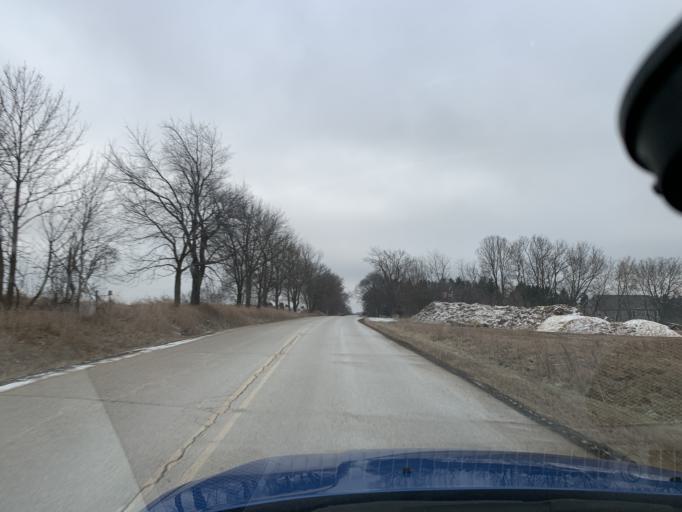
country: US
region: Wisconsin
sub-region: Dane County
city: Middleton
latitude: 43.0718
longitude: -89.5714
